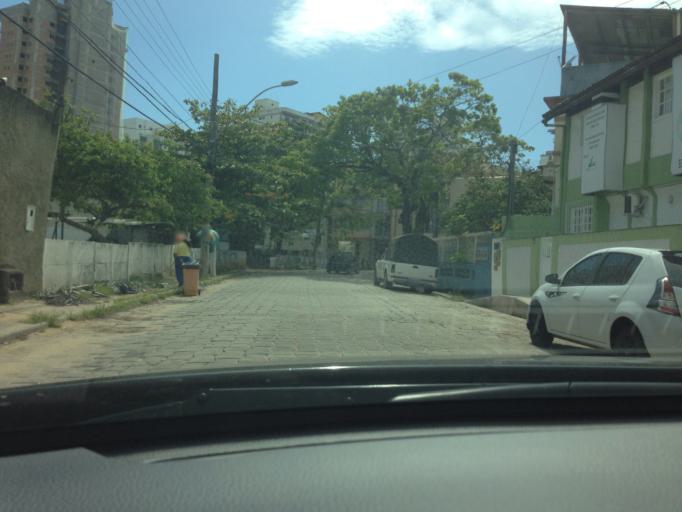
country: BR
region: Espirito Santo
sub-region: Guarapari
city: Guarapari
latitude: -20.6735
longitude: -40.5029
